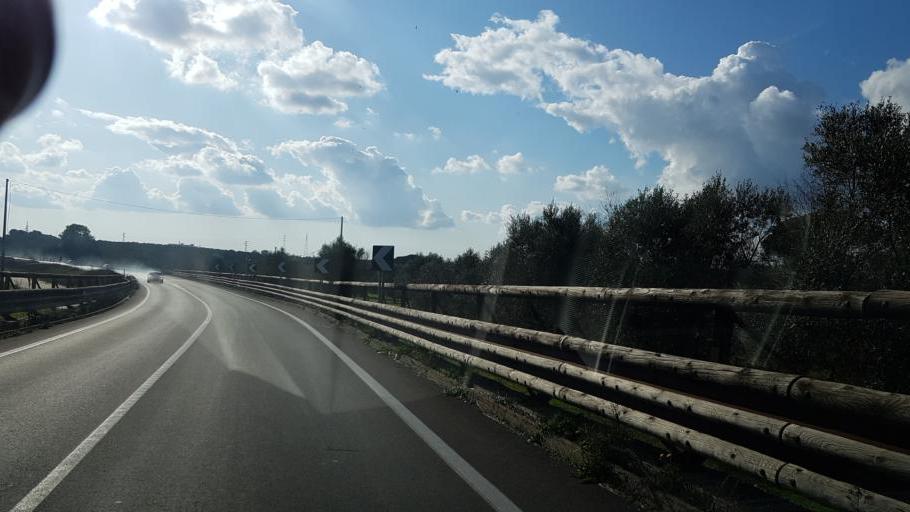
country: IT
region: Apulia
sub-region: Provincia di Lecce
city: Squinzano
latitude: 40.4198
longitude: 18.0257
